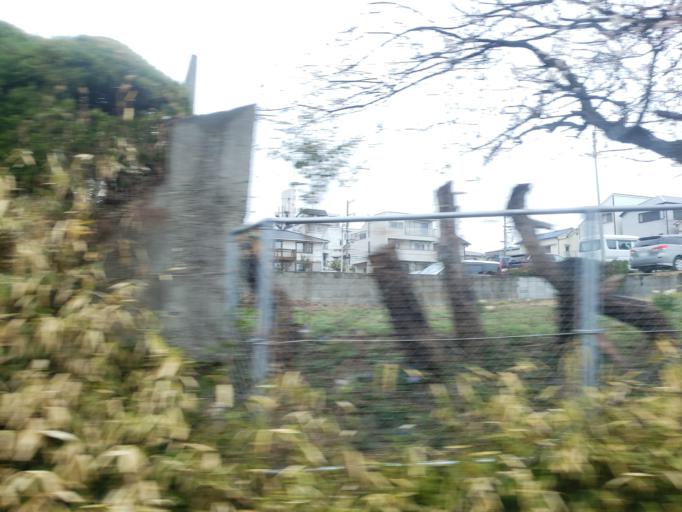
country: JP
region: Hyogo
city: Akashi
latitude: 34.6325
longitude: 135.0399
